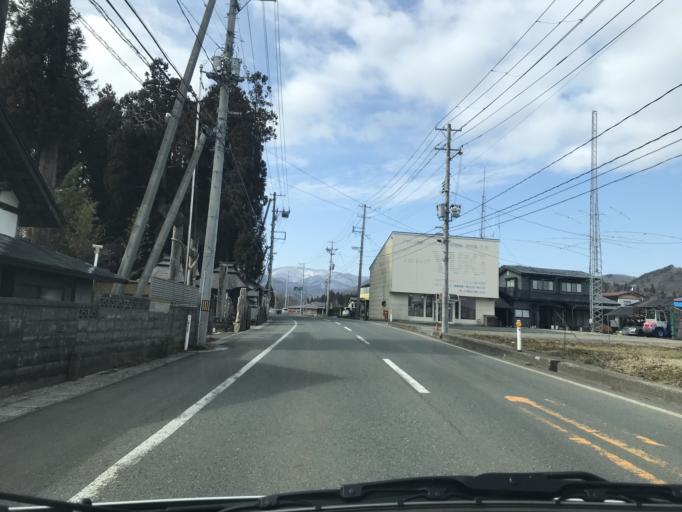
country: JP
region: Iwate
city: Hanamaki
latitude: 39.3982
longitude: 141.0363
